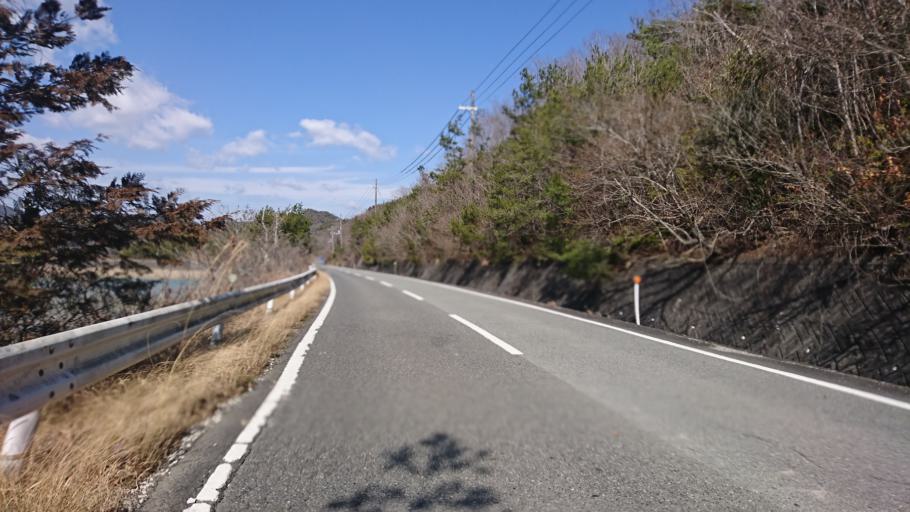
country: JP
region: Hyogo
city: Kakogawacho-honmachi
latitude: 34.8641
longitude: 134.7984
